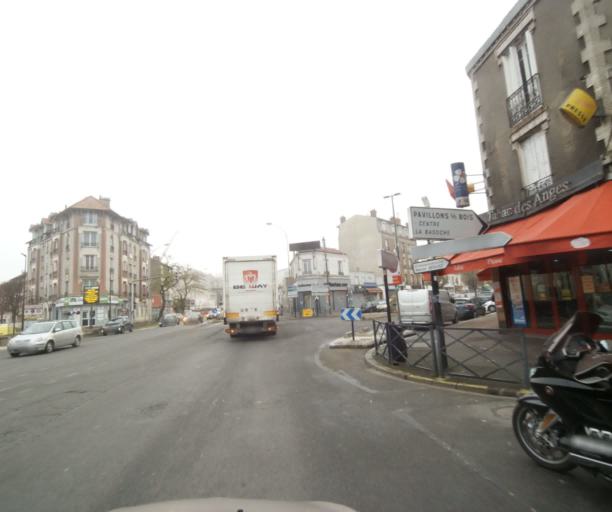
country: FR
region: Ile-de-France
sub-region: Departement de Seine-Saint-Denis
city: Les Pavillons-sous-Bois
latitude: 48.9105
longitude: 2.5121
